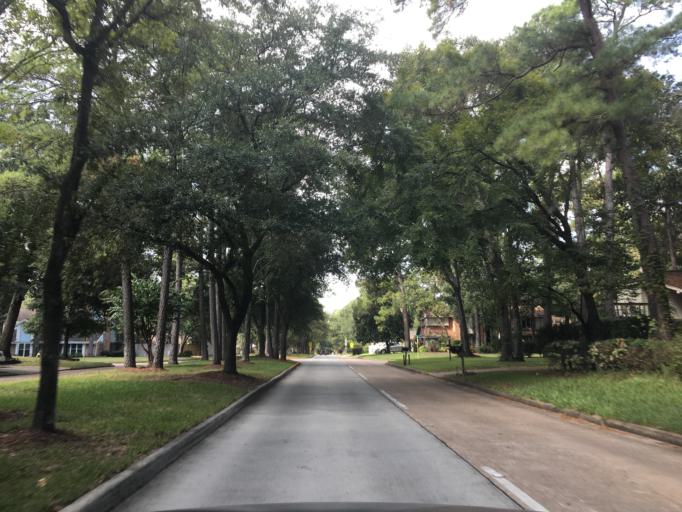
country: US
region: Texas
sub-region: Harris County
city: Spring
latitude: 30.0483
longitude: -95.4400
